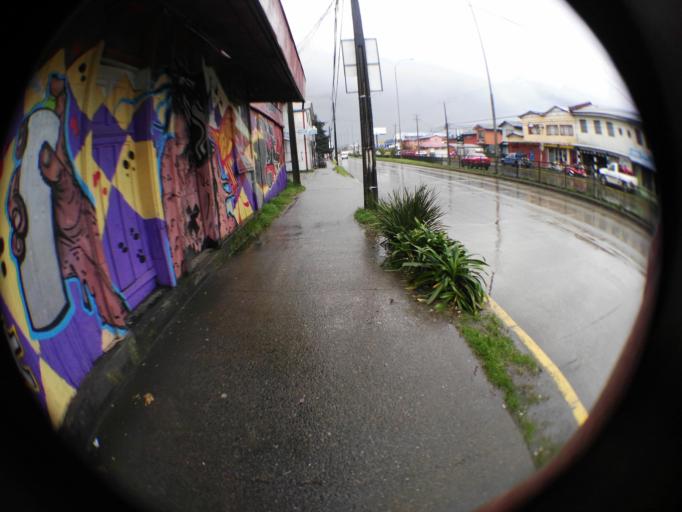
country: CL
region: Los Lagos
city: Las Animas
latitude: -39.8262
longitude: -73.2244
